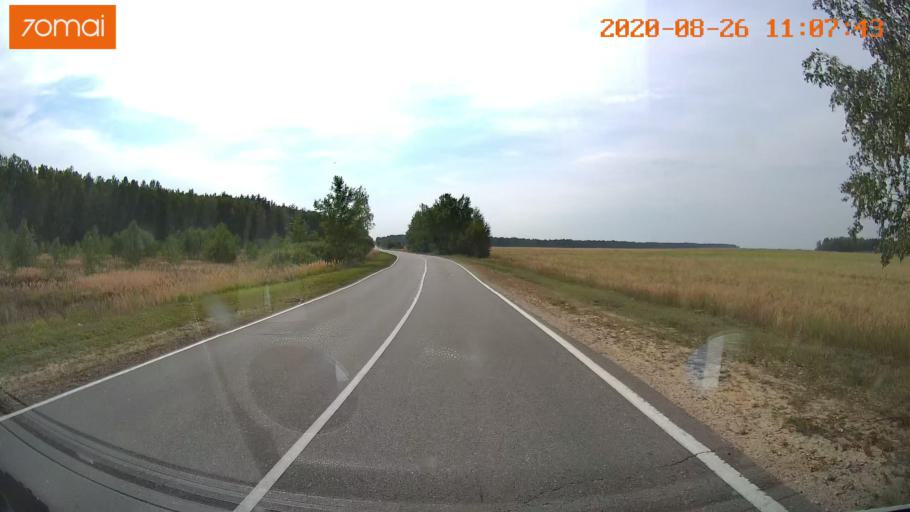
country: RU
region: Rjazan
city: Izhevskoye
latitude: 54.5154
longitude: 41.1205
